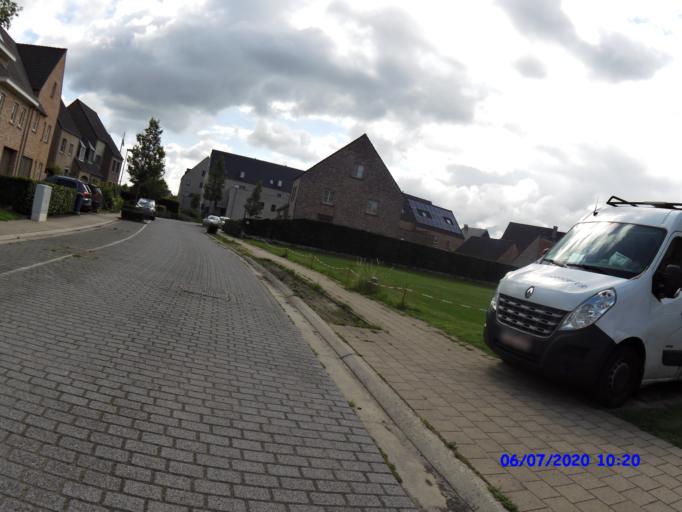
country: BE
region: Flanders
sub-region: Provincie Antwerpen
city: Oud-Turnhout
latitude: 51.3161
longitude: 4.9763
